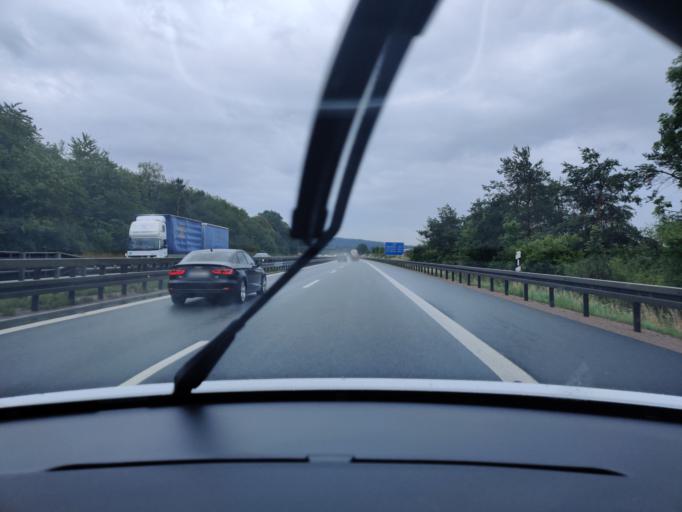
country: DE
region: Bavaria
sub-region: Upper Palatinate
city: Pfreimd
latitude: 49.5107
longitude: 12.1730
